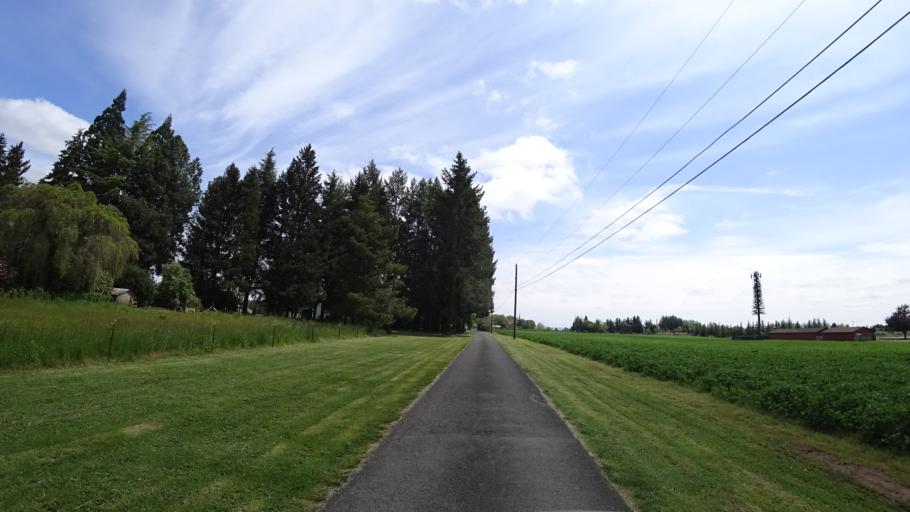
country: US
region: Oregon
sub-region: Washington County
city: Hillsboro
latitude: 45.5534
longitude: -122.9950
